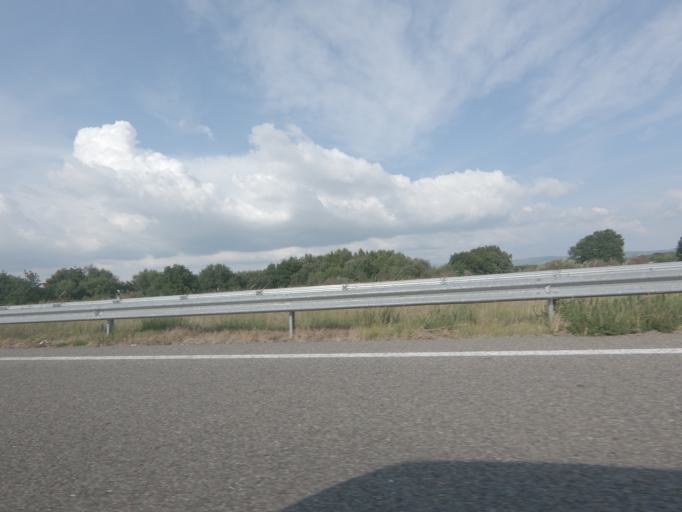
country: ES
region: Galicia
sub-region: Provincia de Ourense
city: Xinzo de Limia
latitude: 42.1198
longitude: -7.7388
